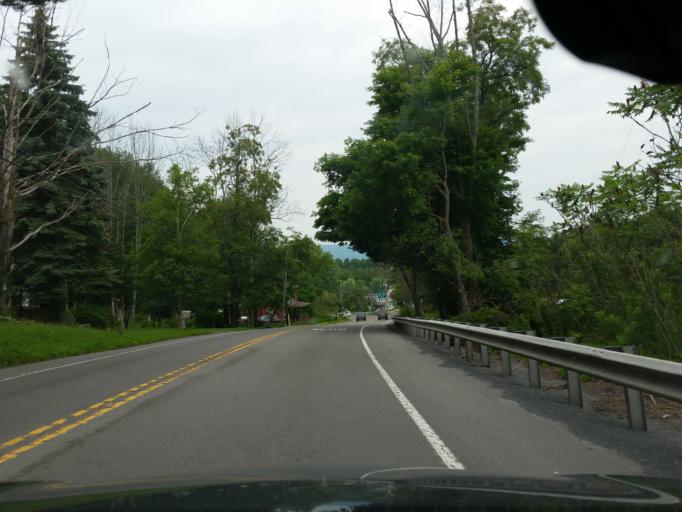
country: US
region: Pennsylvania
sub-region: Centre County
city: Centre Hall
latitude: 40.7926
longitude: -77.6239
